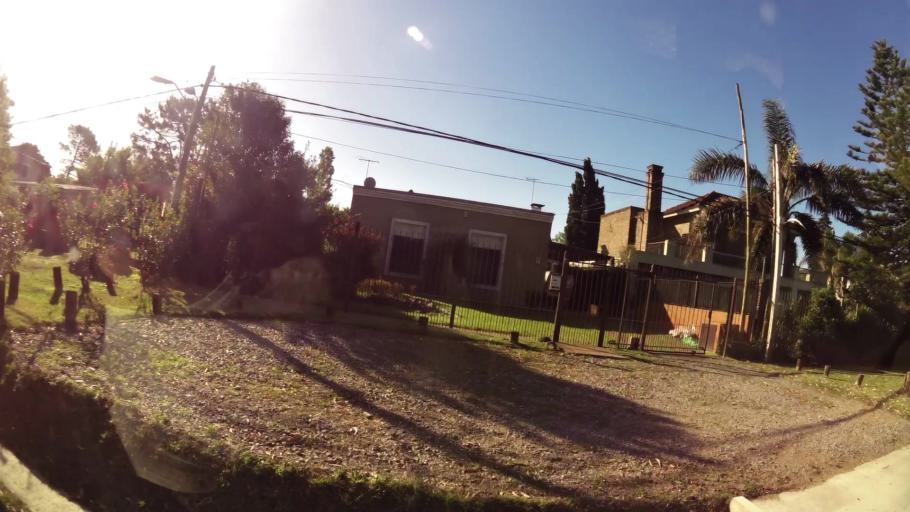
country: UY
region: Canelones
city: Barra de Carrasco
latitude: -34.8630
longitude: -56.0330
